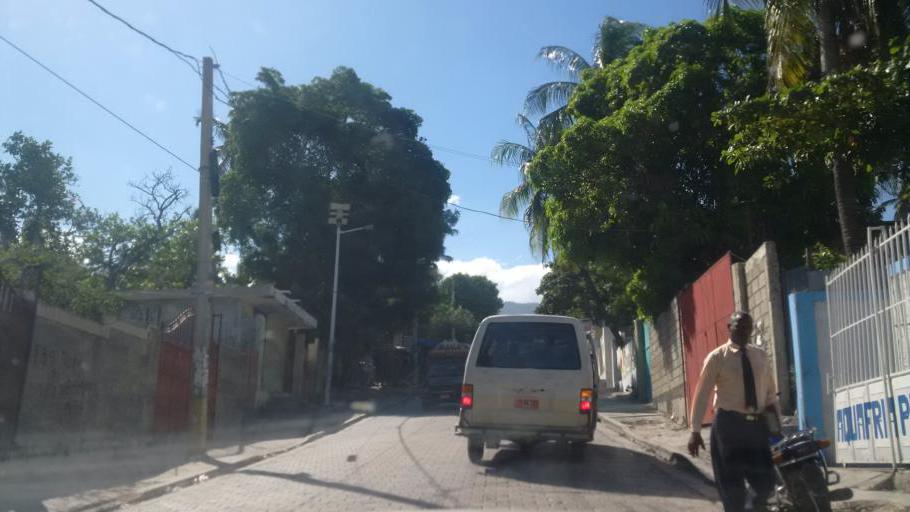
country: HT
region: Ouest
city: Port-au-Prince
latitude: 18.5453
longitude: -72.3220
